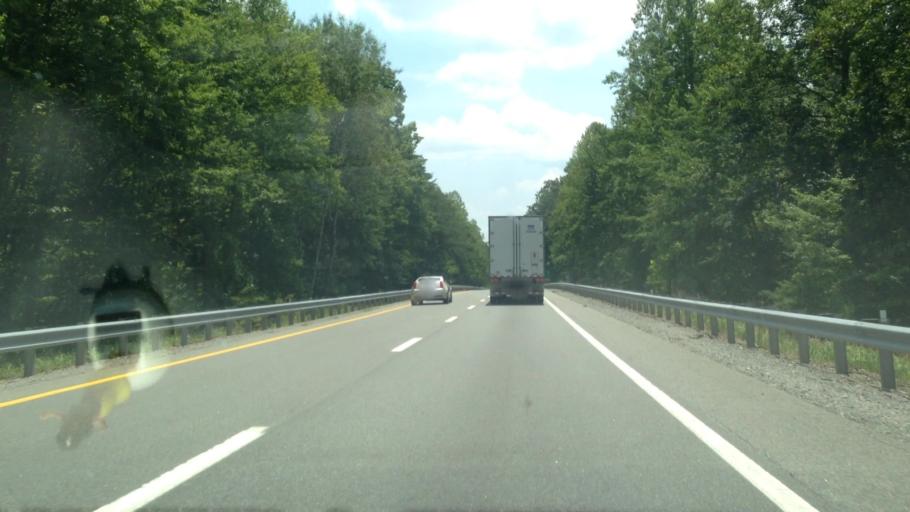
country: US
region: Virginia
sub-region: Henry County
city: Horse Pasture
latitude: 36.6391
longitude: -79.8953
